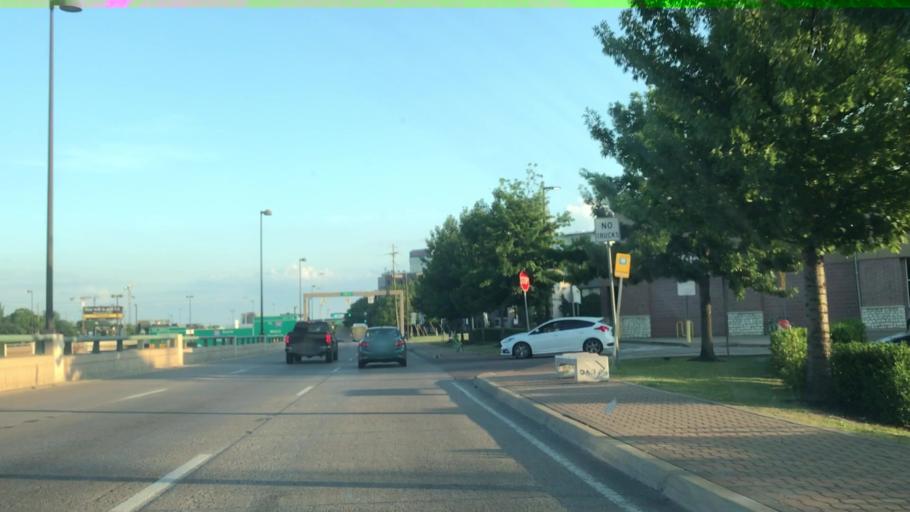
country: US
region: Texas
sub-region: Dallas County
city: Dallas
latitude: 32.8011
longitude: -96.7935
